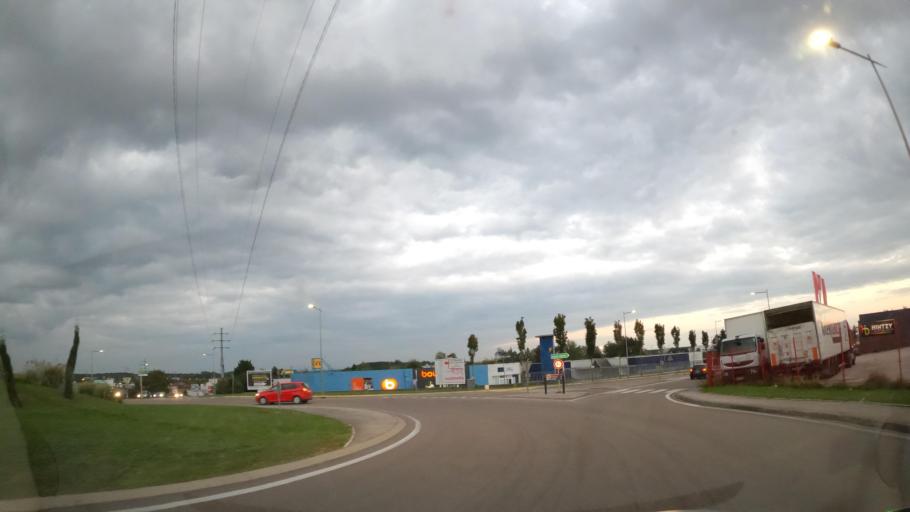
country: FR
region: Franche-Comte
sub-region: Departement du Jura
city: Dole
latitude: 47.1105
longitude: 5.4998
